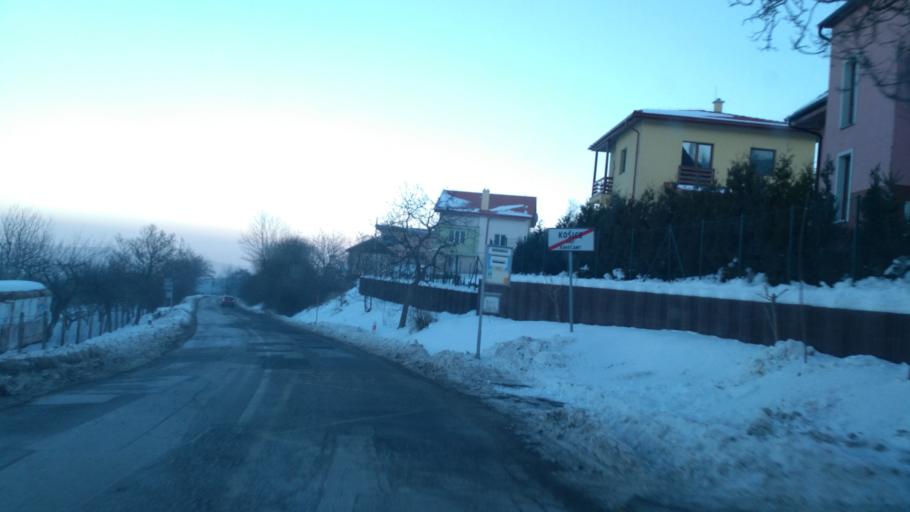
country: SK
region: Kosicky
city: Kosice
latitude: 48.7717
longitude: 21.2139
